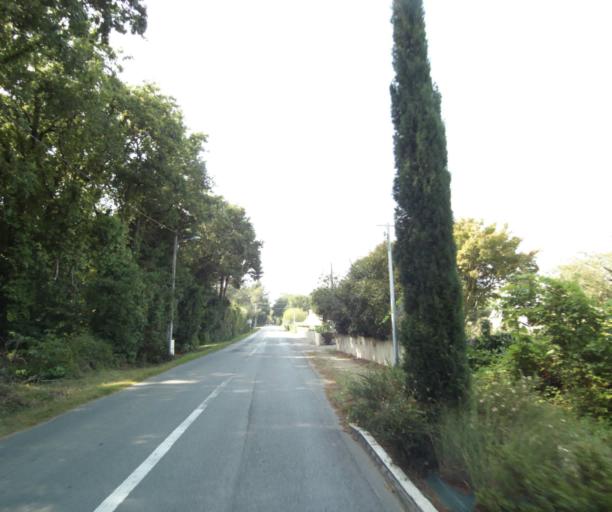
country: FR
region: Brittany
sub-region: Departement du Morbihan
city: Merlevenez
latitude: 47.7042
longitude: -3.2629
